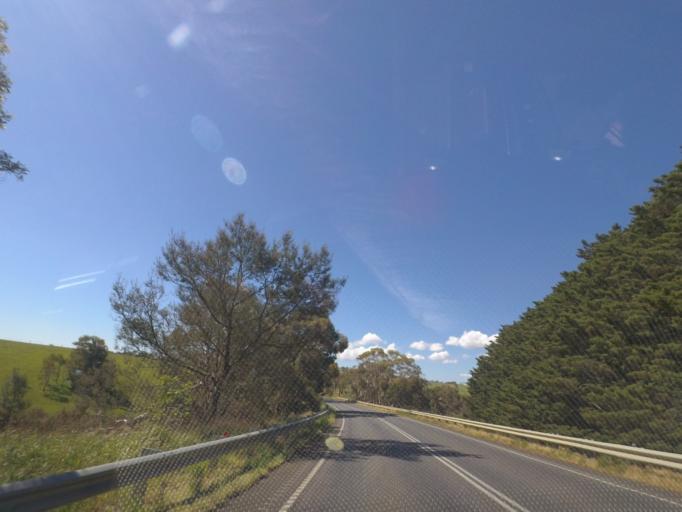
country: AU
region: Victoria
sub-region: Moorabool
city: Bacchus Marsh
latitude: -37.7953
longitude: 144.2127
